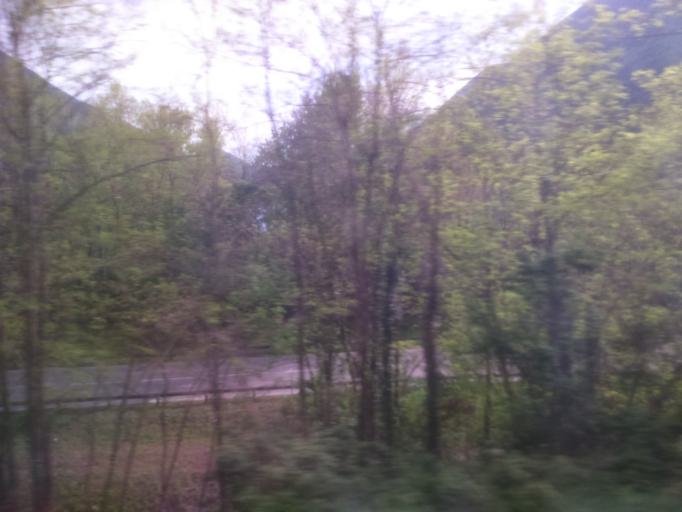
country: FR
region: Rhone-Alpes
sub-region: Departement de l'Isere
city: Saint-Georges-de-Commiers
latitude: 45.0440
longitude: 5.6967
